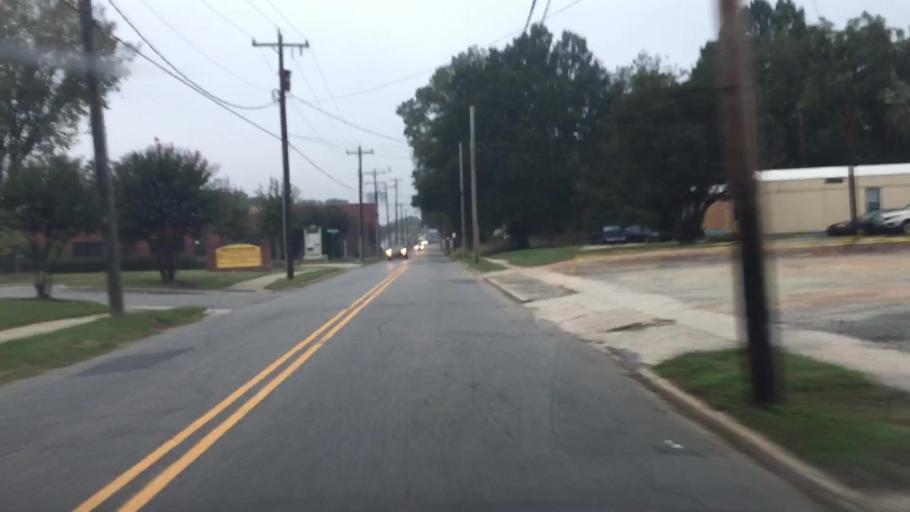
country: US
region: North Carolina
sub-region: Iredell County
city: Mooresville
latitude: 35.5921
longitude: -80.8058
